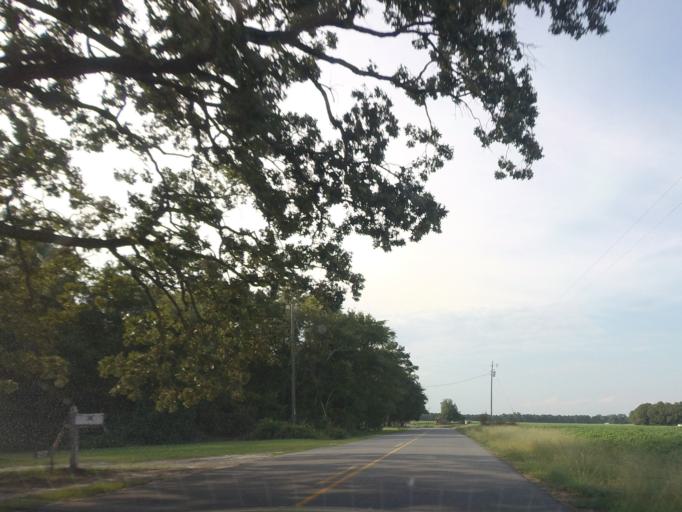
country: US
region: Georgia
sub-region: Bleckley County
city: Cochran
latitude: 32.5233
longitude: -83.3071
